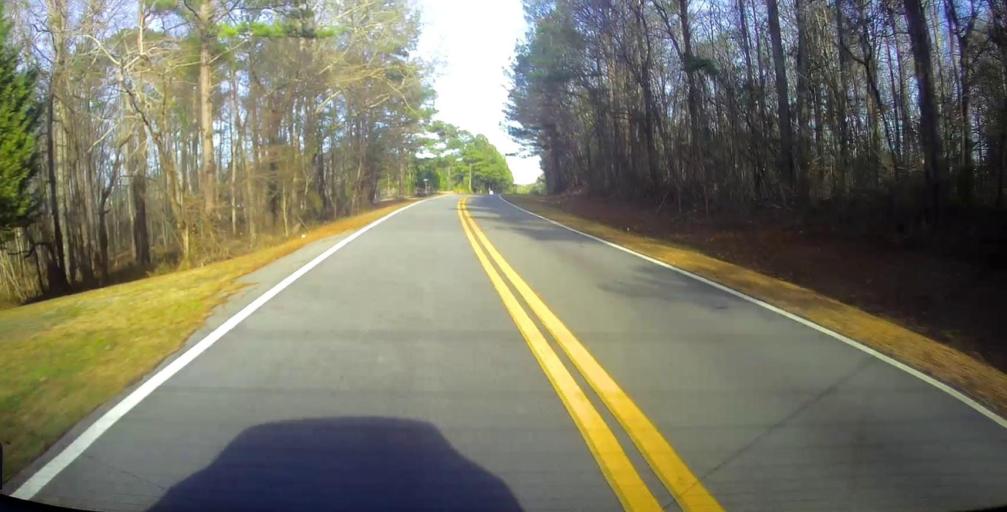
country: US
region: Georgia
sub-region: Bibb County
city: West Point
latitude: 32.8343
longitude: -83.9273
